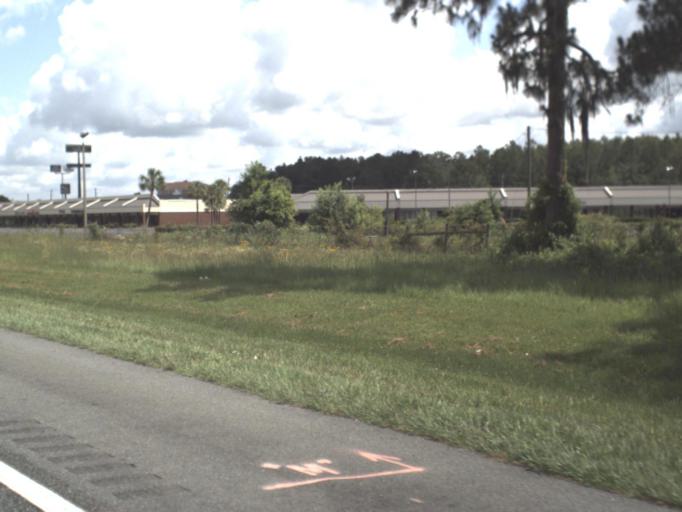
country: US
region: Florida
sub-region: Columbia County
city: Lake City
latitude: 30.1733
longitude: -82.6851
